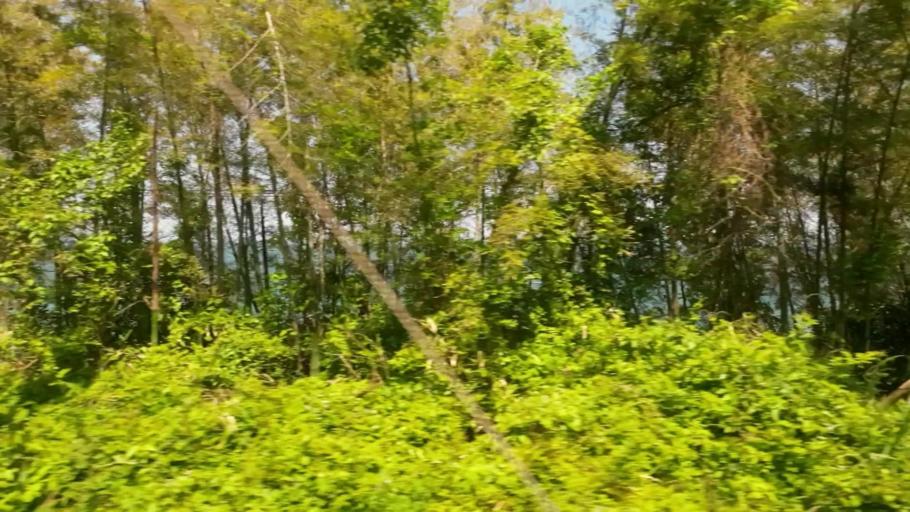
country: JP
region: Ehime
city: Hojo
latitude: 34.0066
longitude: 132.7835
